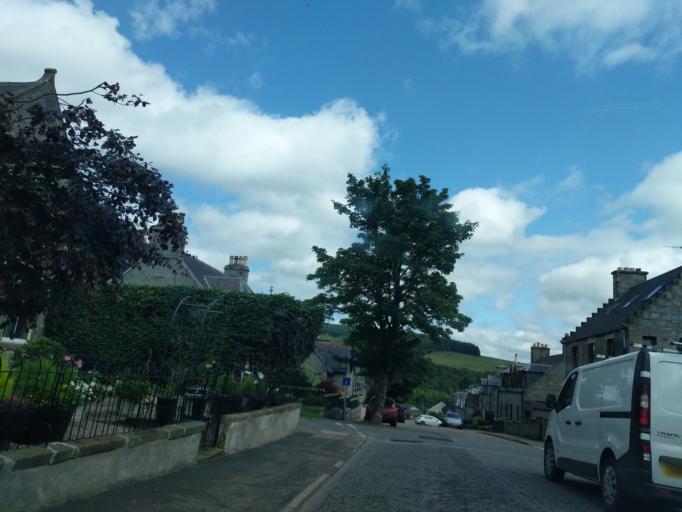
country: GB
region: Scotland
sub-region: Moray
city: Dufftown
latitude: 57.4462
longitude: -3.1256
